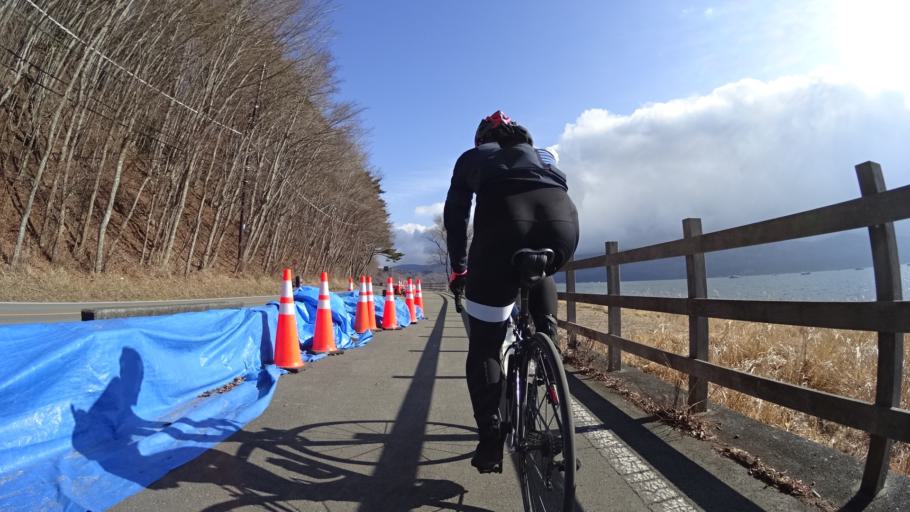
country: JP
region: Shizuoka
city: Gotemba
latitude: 35.4285
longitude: 138.8614
